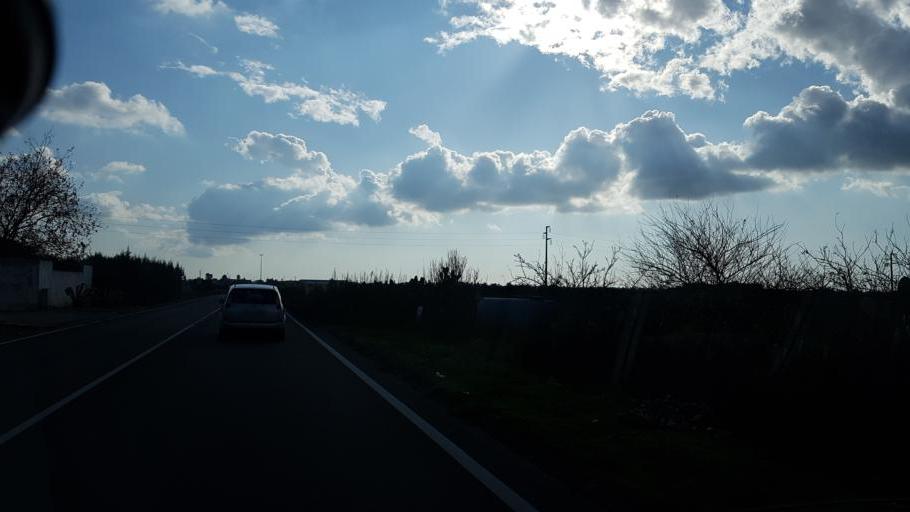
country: IT
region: Apulia
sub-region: Provincia di Lecce
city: Veglie
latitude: 40.3542
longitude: 17.9684
